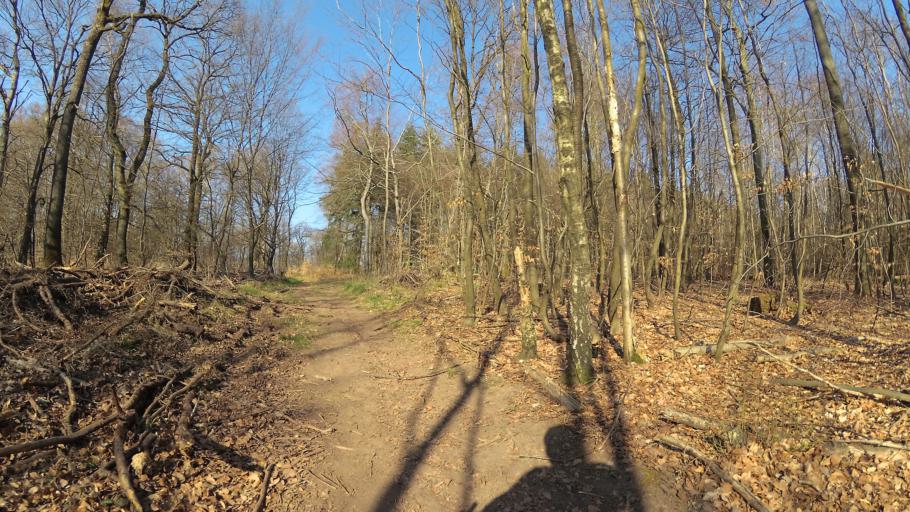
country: DE
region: Saarland
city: Ottweiler
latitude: 49.3894
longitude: 7.1547
